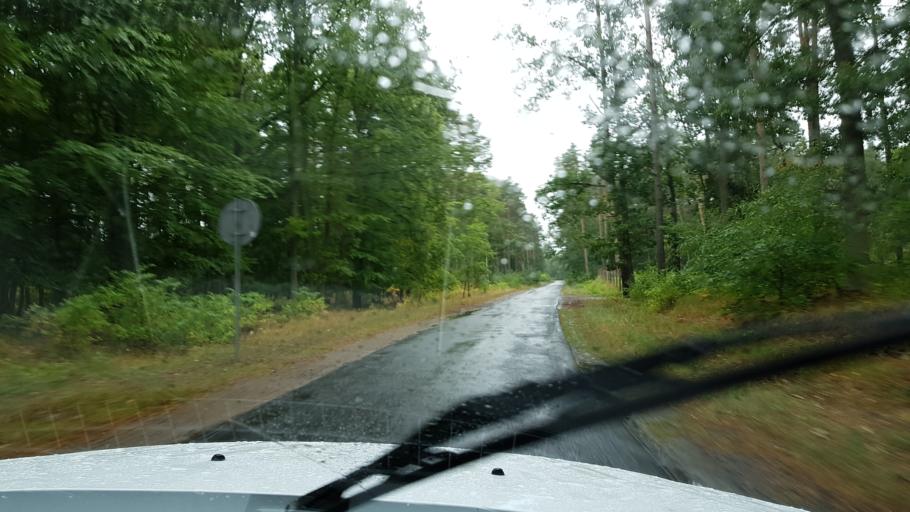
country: DE
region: Brandenburg
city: Schoneberg
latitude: 52.9697
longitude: 14.2080
